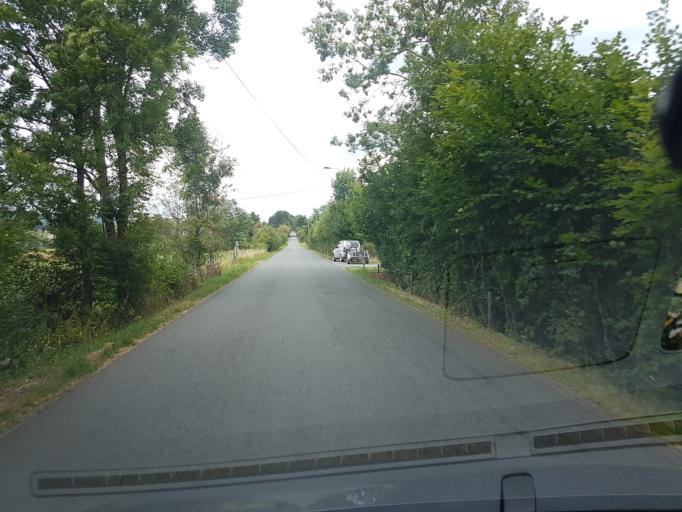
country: BE
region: Wallonia
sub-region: Province du Luxembourg
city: Manhay
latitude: 50.2856
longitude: 5.6691
